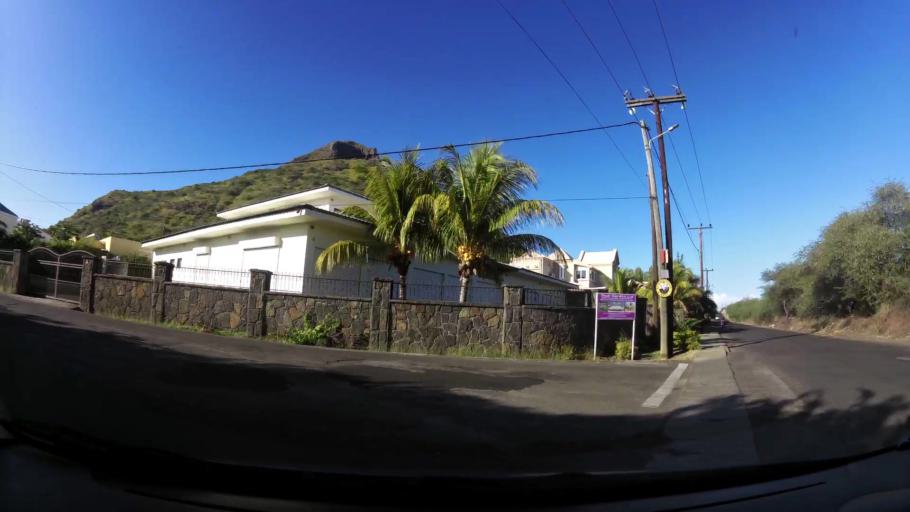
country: MU
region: Black River
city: Tamarin
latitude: -20.3373
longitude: 57.3703
